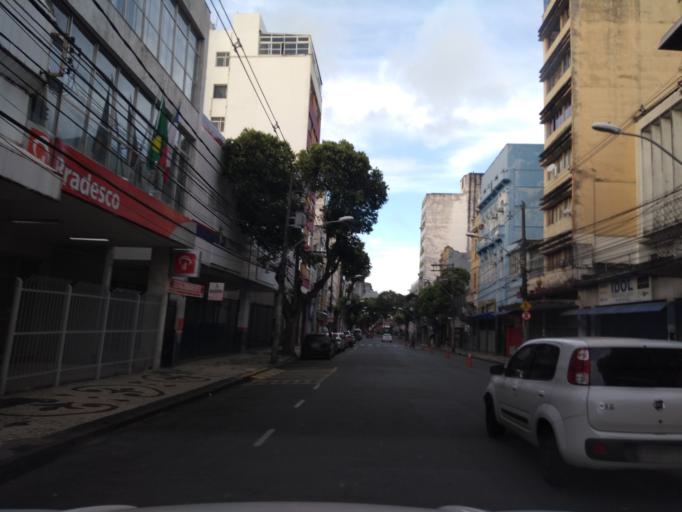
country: BR
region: Bahia
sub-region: Salvador
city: Salvador
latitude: -12.9840
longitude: -38.5169
